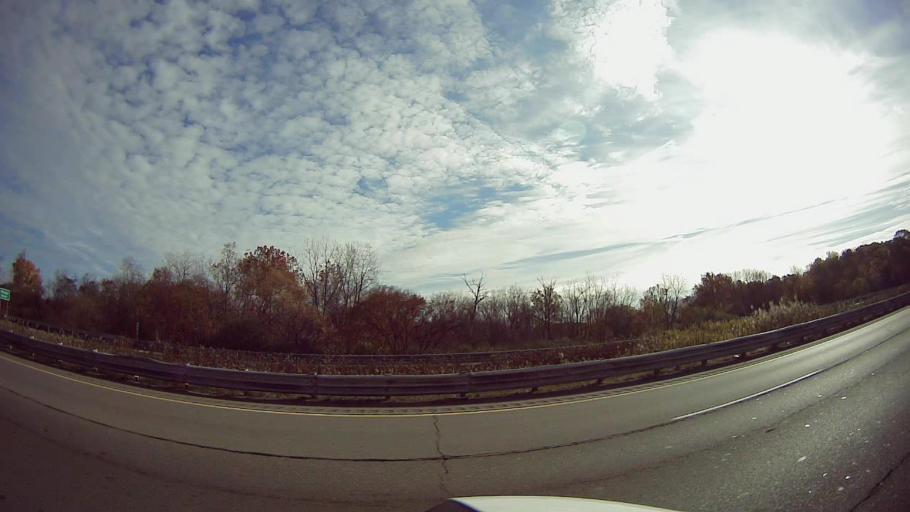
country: US
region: Michigan
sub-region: Wayne County
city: Plymouth
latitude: 42.3710
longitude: -83.4367
